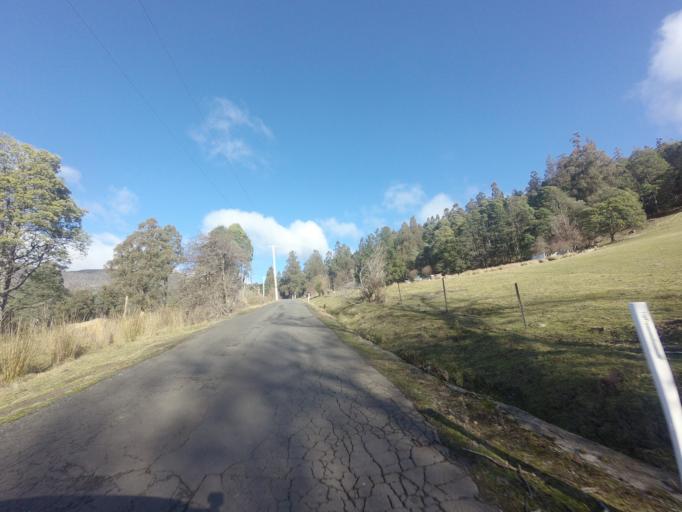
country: AU
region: Tasmania
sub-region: Glenorchy
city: Berriedale
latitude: -42.8510
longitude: 147.1680
